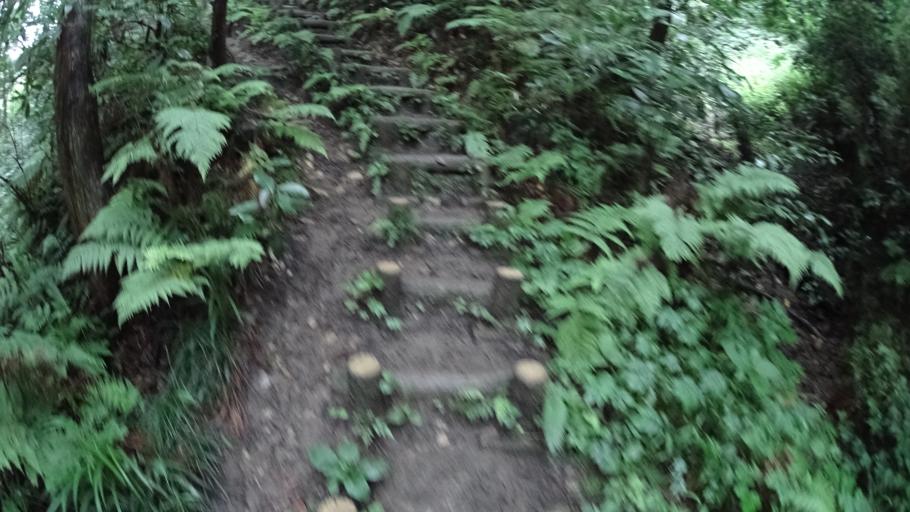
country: JP
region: Kanagawa
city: Yokosuka
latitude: 35.2546
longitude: 139.6340
